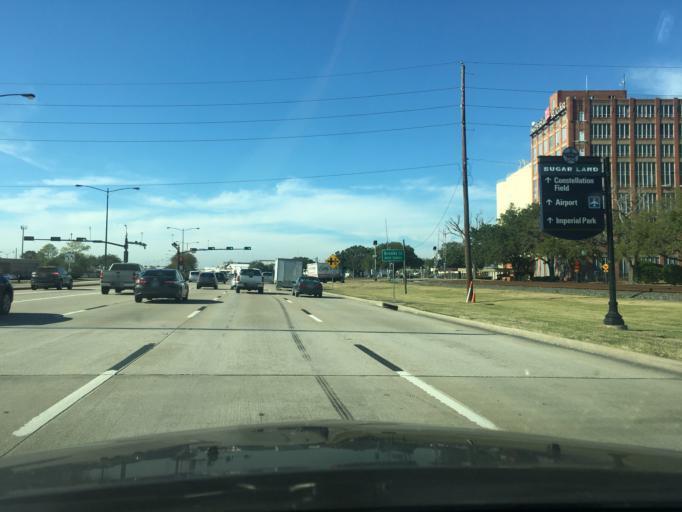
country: US
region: Texas
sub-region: Fort Bend County
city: Sugar Land
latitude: 29.6203
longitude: -95.6341
